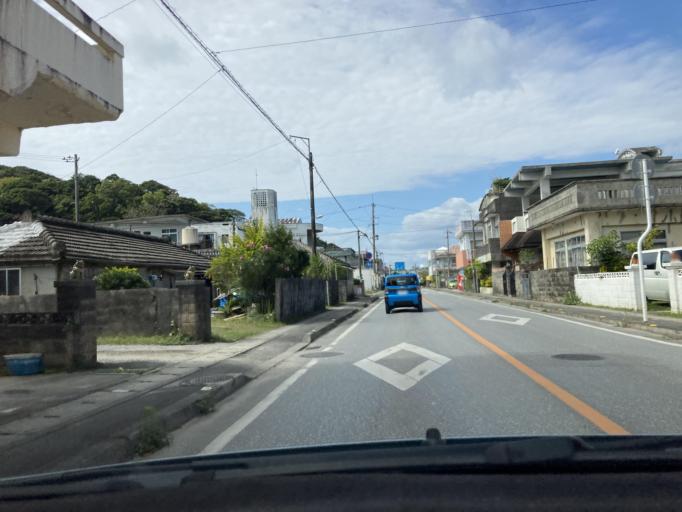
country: JP
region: Okinawa
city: Nago
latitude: 26.6579
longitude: 127.9015
